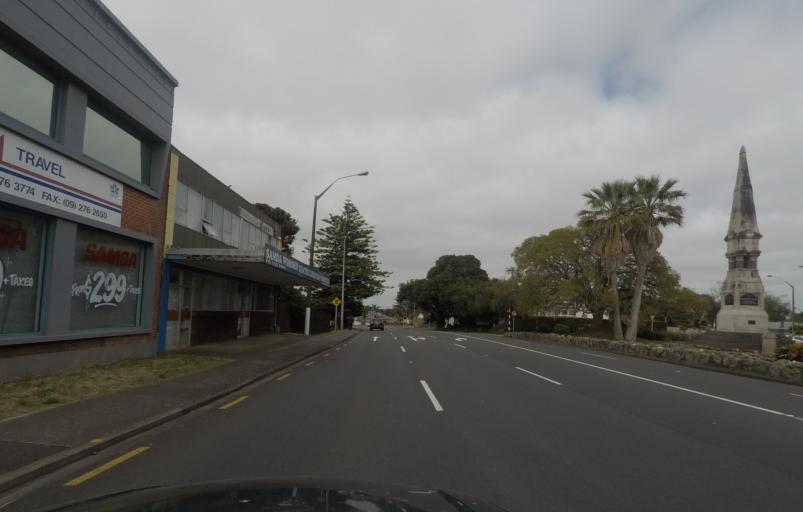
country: NZ
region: Auckland
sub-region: Auckland
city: Mangere
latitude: -36.9498
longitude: 174.8452
